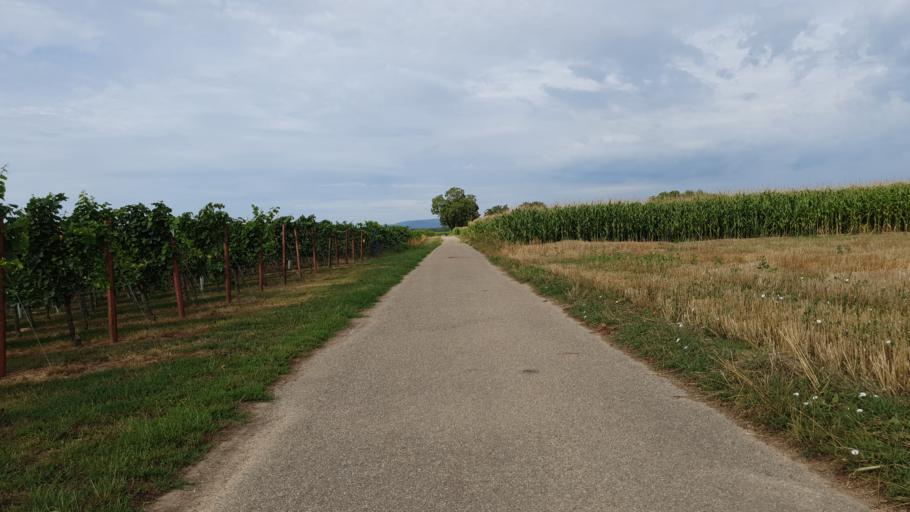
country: DE
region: Rheinland-Pfalz
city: Hergersweiler
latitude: 49.1143
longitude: 8.0994
